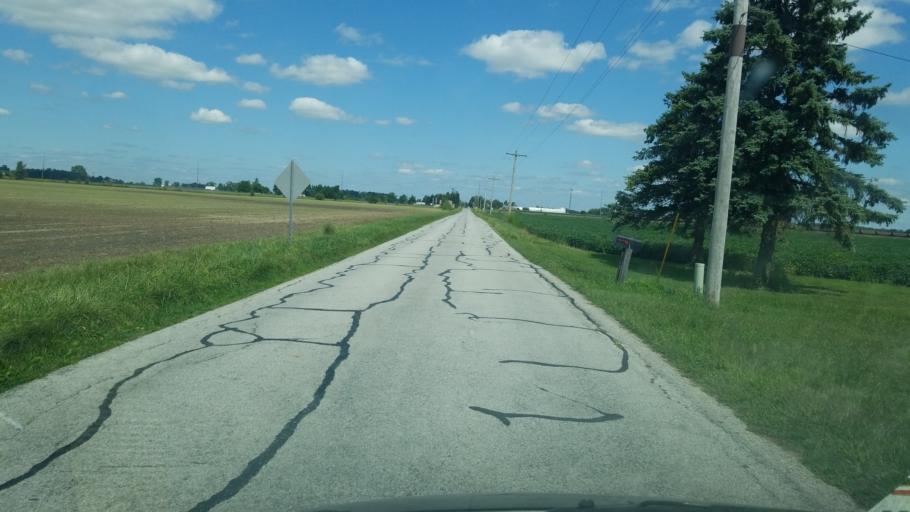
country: US
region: Ohio
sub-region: Fulton County
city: Swanton
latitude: 41.5749
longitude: -83.9408
